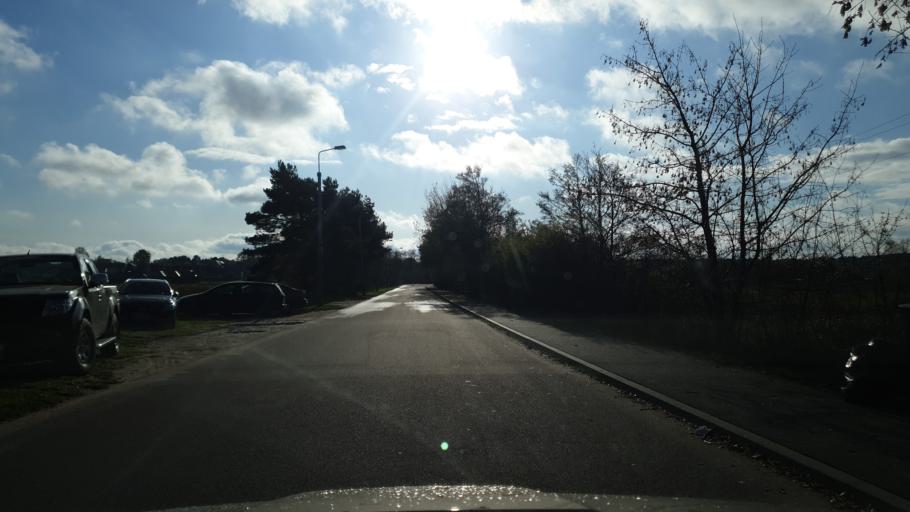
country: PL
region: Pomeranian Voivodeship
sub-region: Powiat pucki
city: Jastrzebia Gora
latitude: 54.8301
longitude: 18.2445
